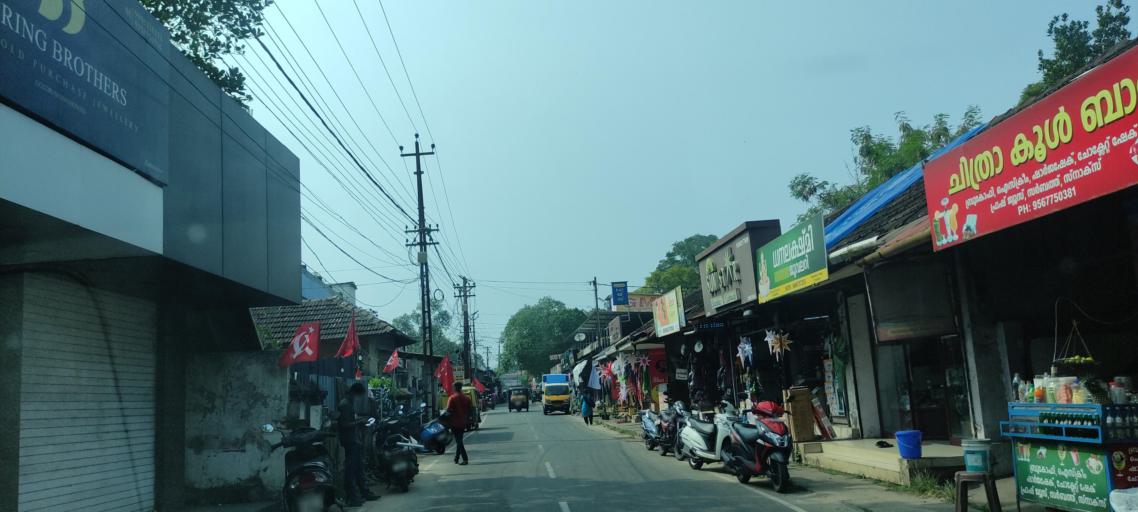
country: IN
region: Kerala
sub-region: Alappuzha
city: Vayalar
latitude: 9.6866
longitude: 76.3380
